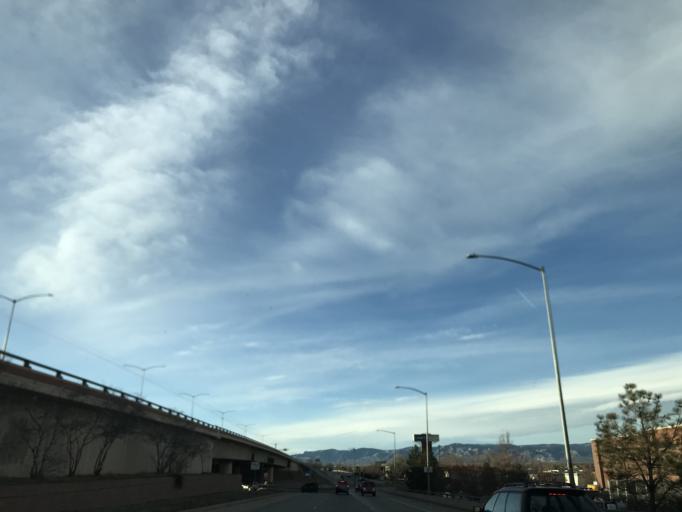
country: US
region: Colorado
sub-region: Arapahoe County
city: Littleton
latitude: 39.6255
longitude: -105.0127
